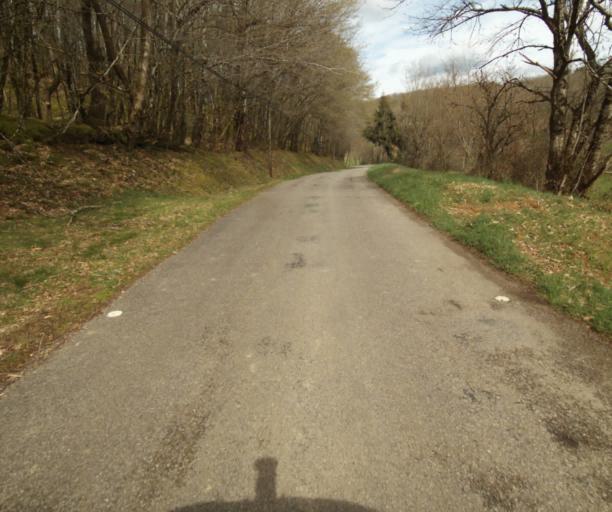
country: FR
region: Limousin
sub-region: Departement de la Correze
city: Laguenne
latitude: 45.2324
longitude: 1.8526
